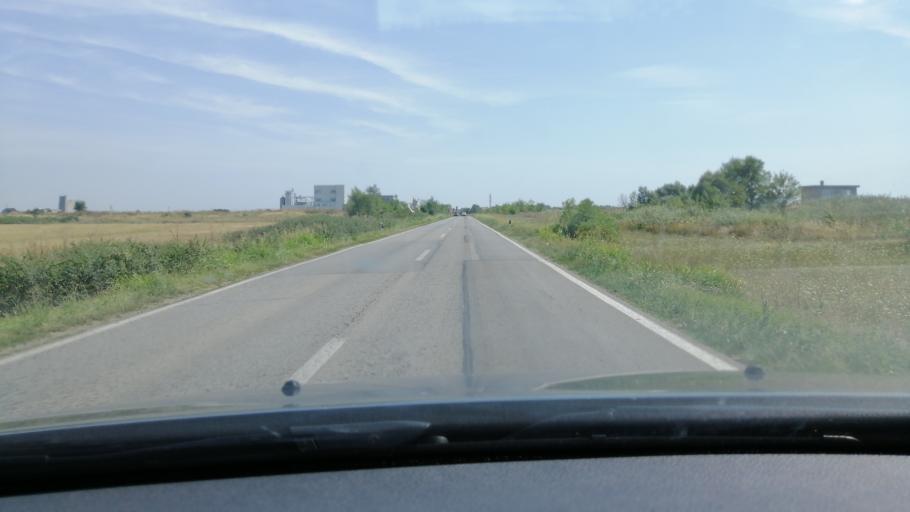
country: RS
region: Autonomna Pokrajina Vojvodina
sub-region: Srednjebanatski Okrug
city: Secanj
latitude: 45.3718
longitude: 20.7500
